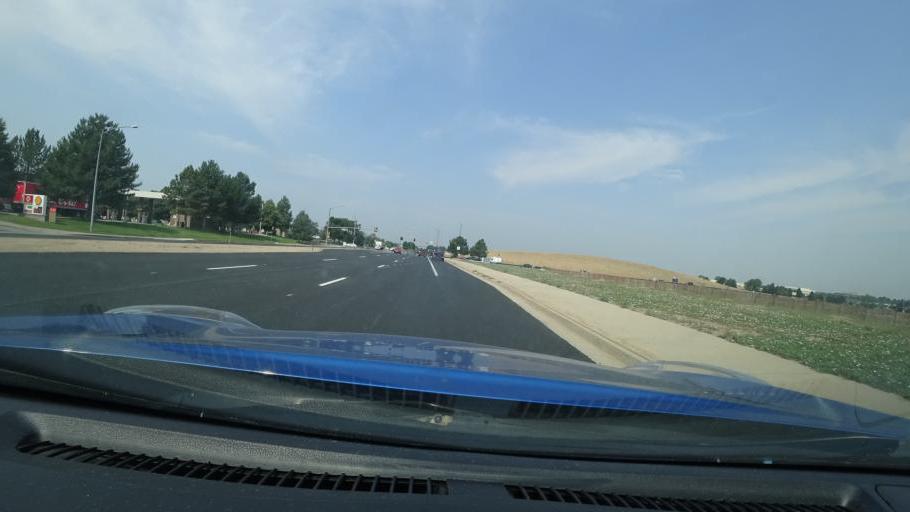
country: US
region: Colorado
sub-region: Adams County
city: Aurora
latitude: 39.7065
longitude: -104.7893
